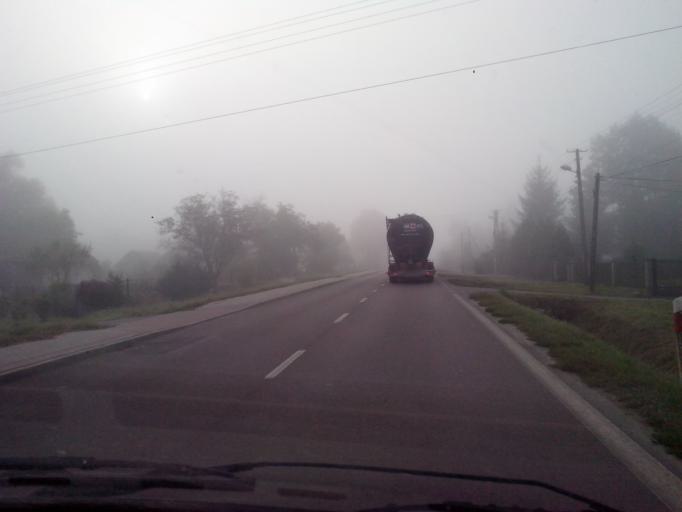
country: PL
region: Subcarpathian Voivodeship
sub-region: Przemysl
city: Przemysl
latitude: 49.7971
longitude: 22.7166
